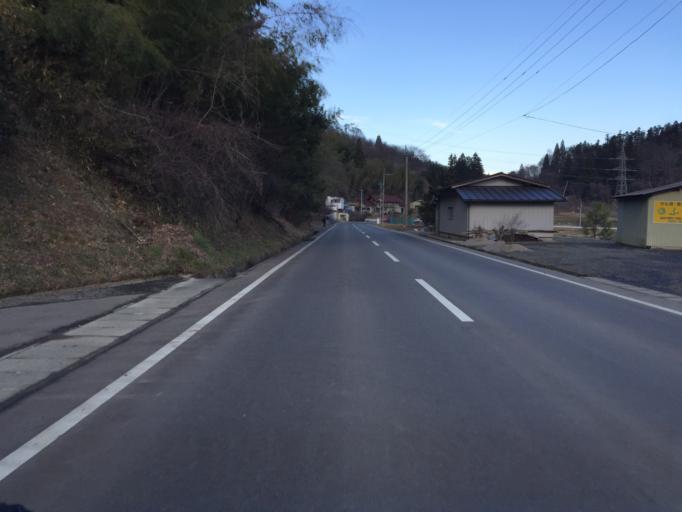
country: JP
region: Fukushima
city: Fukushima-shi
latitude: 37.7080
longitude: 140.4110
